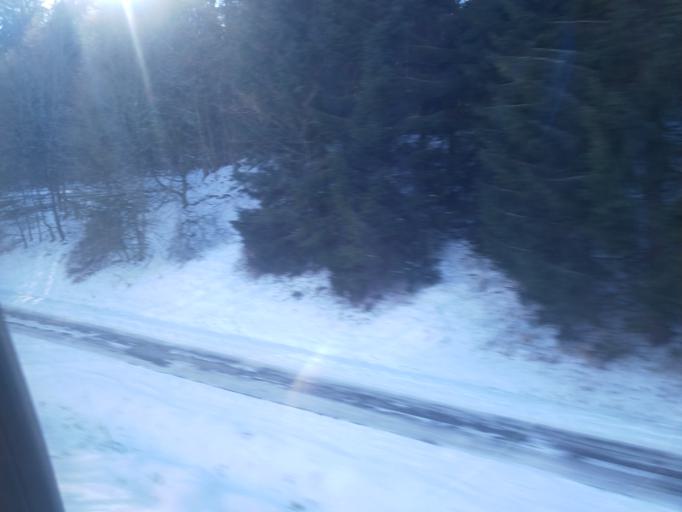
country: DE
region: Baden-Wuerttemberg
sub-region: Freiburg Region
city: Frittlingen
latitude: 48.1268
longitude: 8.6692
